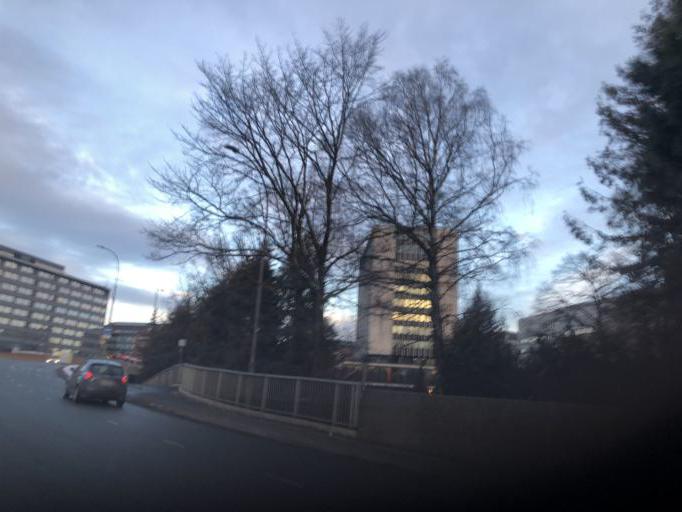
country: NO
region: Oslo
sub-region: Oslo
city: Oslo
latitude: 59.9127
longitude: 10.8035
